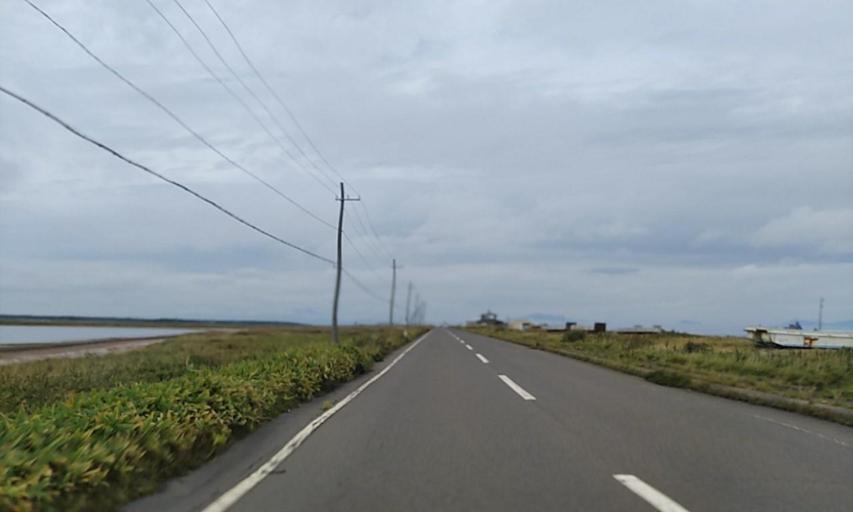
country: JP
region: Hokkaido
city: Shibetsu
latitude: 43.5947
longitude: 145.3272
